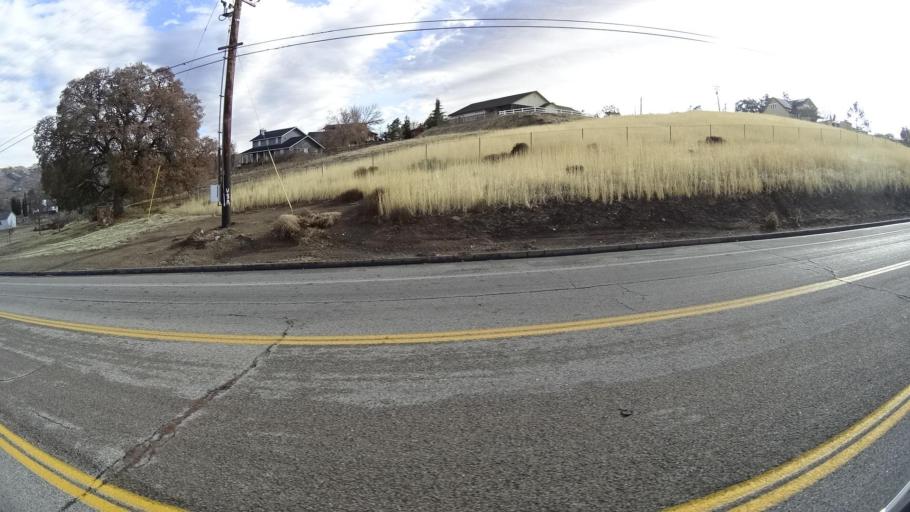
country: US
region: California
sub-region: Kern County
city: Golden Hills
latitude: 35.1429
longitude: -118.4950
